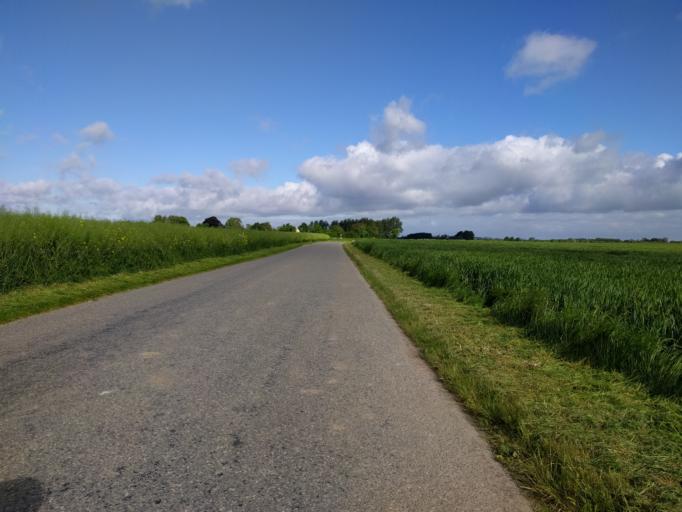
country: DK
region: South Denmark
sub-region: Kerteminde Kommune
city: Kerteminde
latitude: 55.4297
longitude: 10.6278
